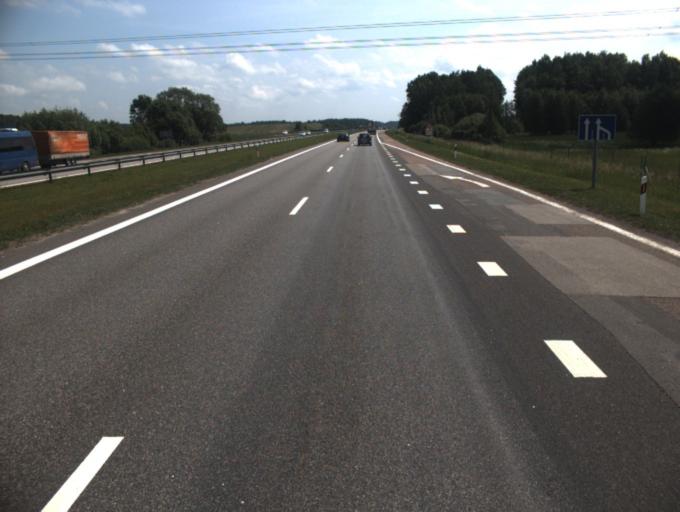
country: LT
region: Klaipedos apskritis
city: Gargzdai
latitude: 55.7073
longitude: 21.5594
